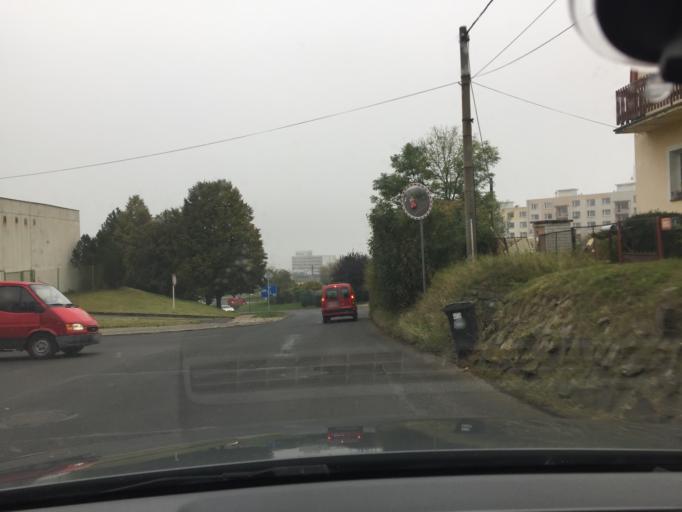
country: CZ
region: Ustecky
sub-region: Okres Usti nad Labem
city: Usti nad Labem
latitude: 50.6804
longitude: 14.0370
